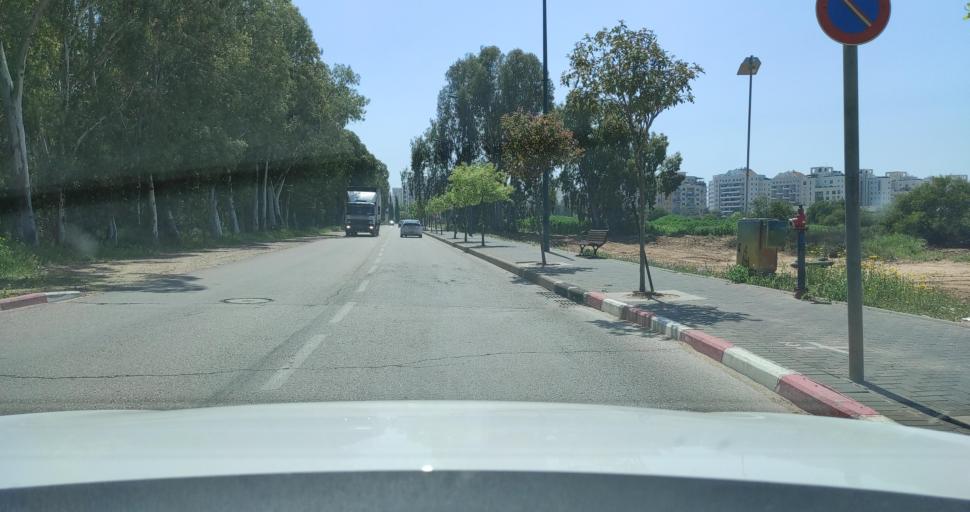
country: IL
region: Central District
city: Nordiyya
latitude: 32.3062
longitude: 34.8743
